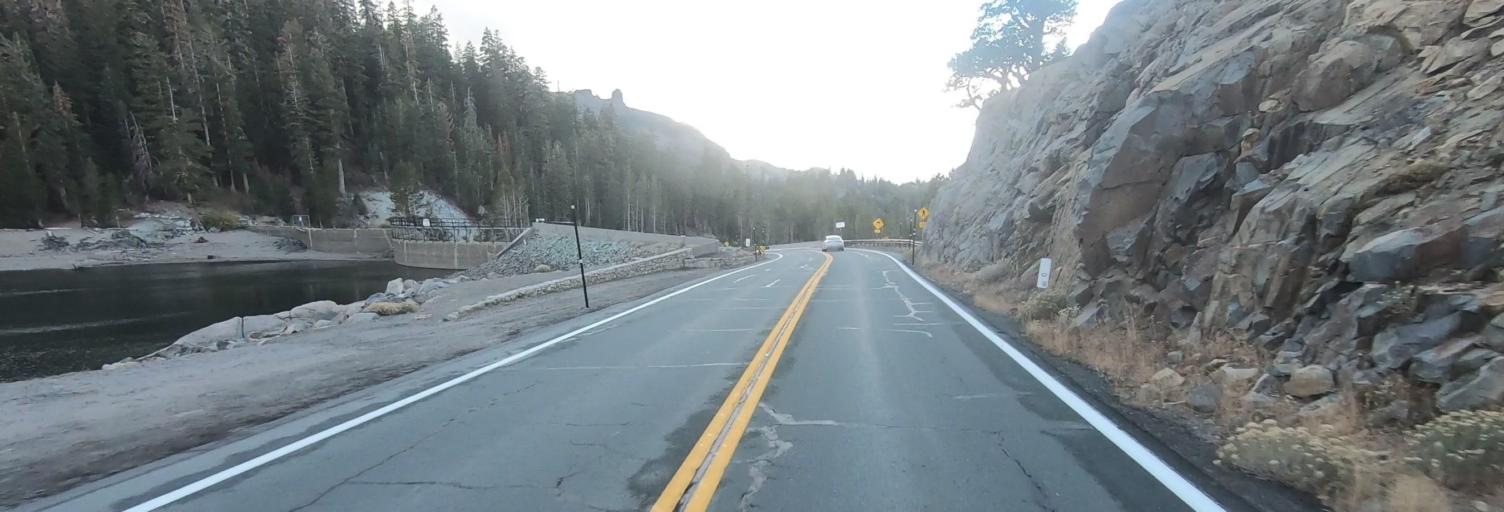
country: US
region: California
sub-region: El Dorado County
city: South Lake Tahoe
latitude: 38.7036
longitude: -120.0634
